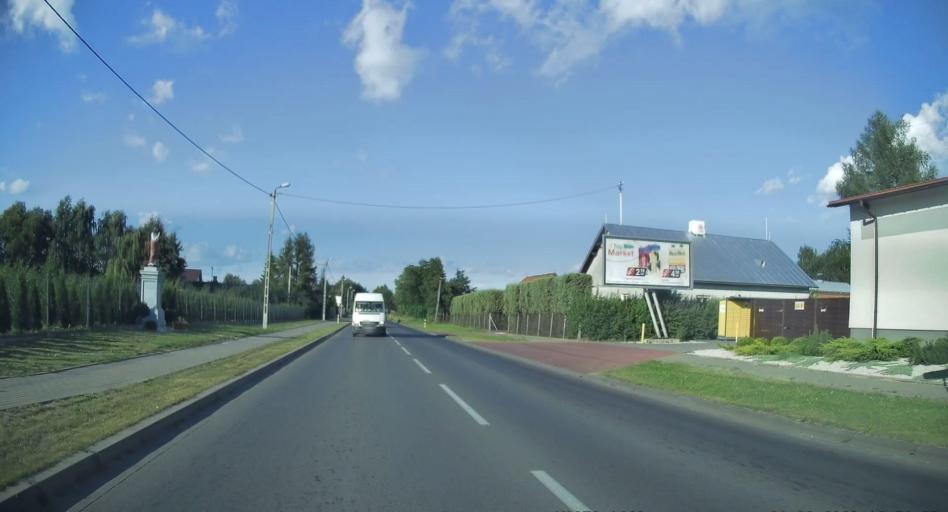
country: PL
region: Masovian Voivodeship
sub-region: Powiat grojecki
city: Belsk Duzy
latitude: 51.8264
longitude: 20.8103
